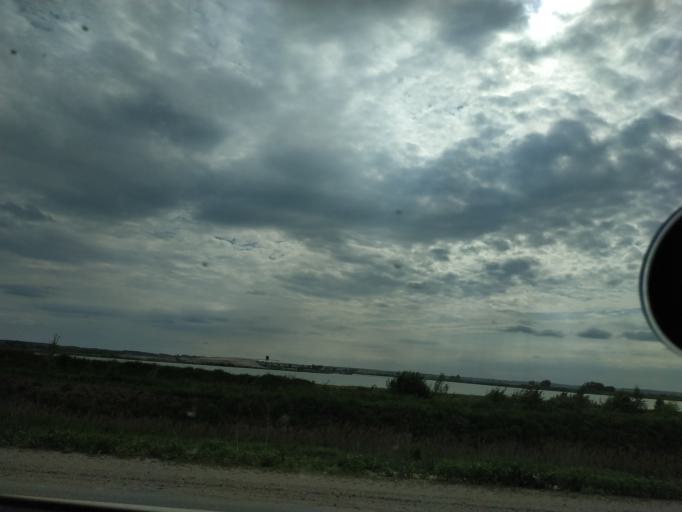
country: RU
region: Moskovskaya
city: Malyshevo
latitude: 55.5094
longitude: 38.2843
